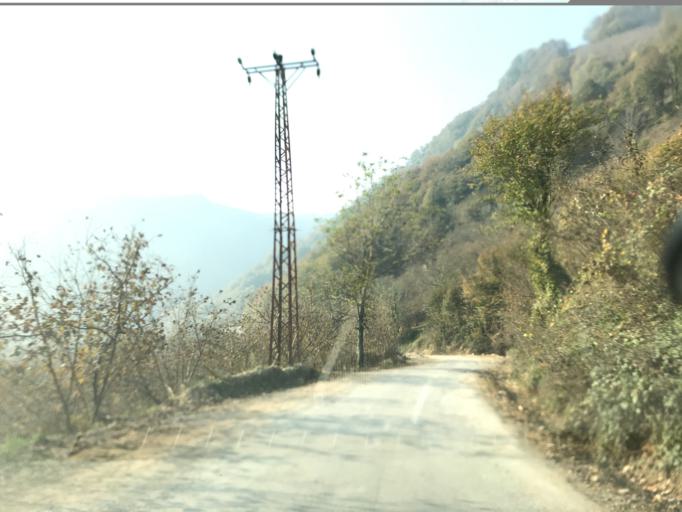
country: TR
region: Duzce
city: Cumayeri
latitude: 40.9349
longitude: 30.9281
